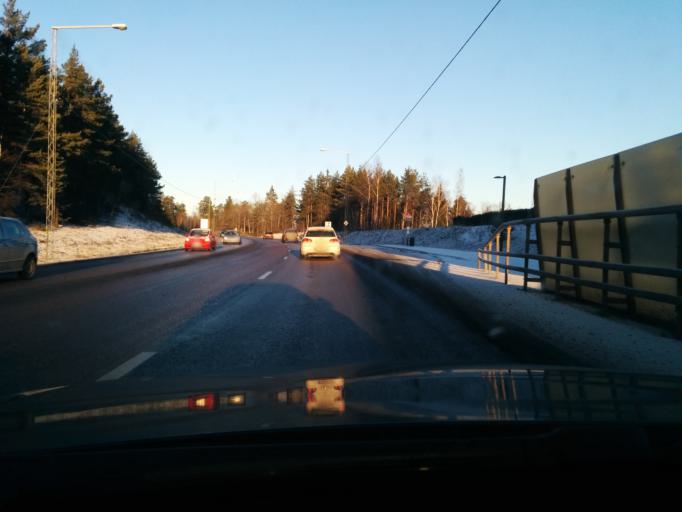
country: SE
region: Stockholm
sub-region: Taby Kommun
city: Taby
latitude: 59.4742
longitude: 18.1200
